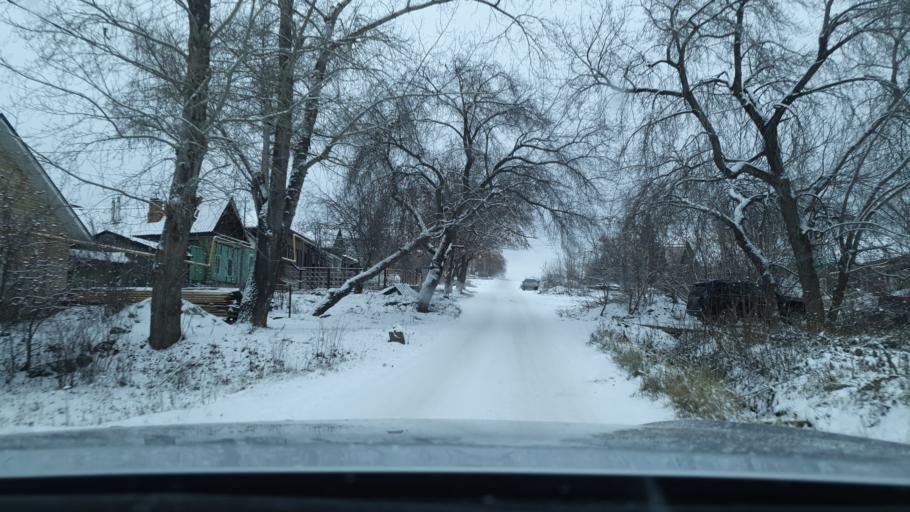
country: RU
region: Sverdlovsk
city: Istok
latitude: 56.7460
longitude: 60.6947
